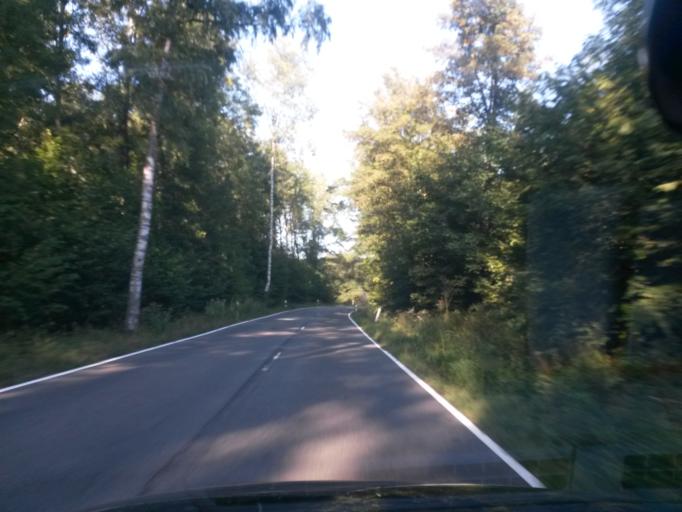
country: DE
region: North Rhine-Westphalia
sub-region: Regierungsbezirk Koln
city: Numbrecht
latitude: 50.9188
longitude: 7.5415
